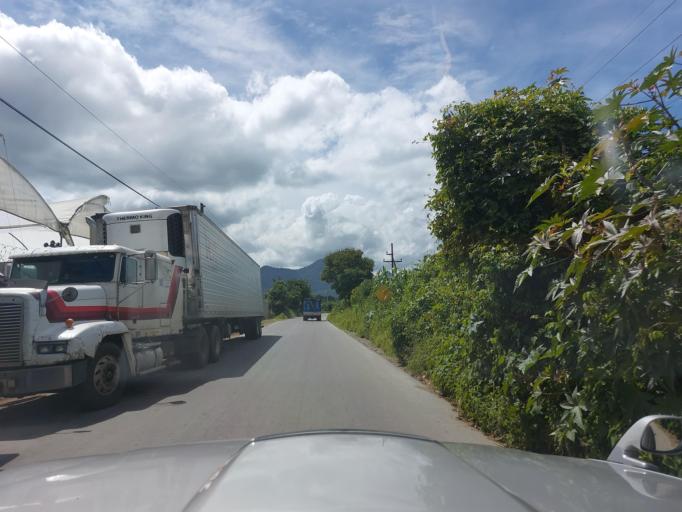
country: GT
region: Chimaltenango
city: San Andres Itzapa
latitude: 14.6161
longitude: -90.8238
